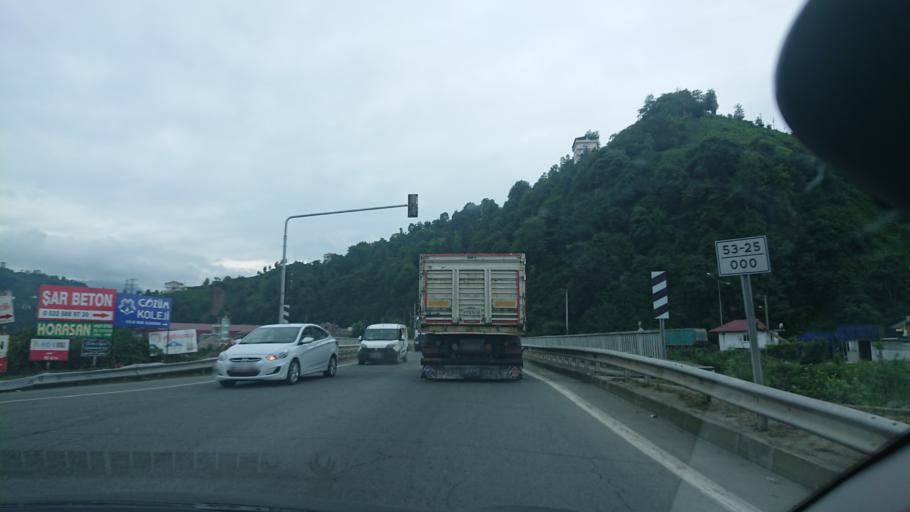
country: TR
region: Rize
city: Gundogdu
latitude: 41.0383
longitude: 40.5799
